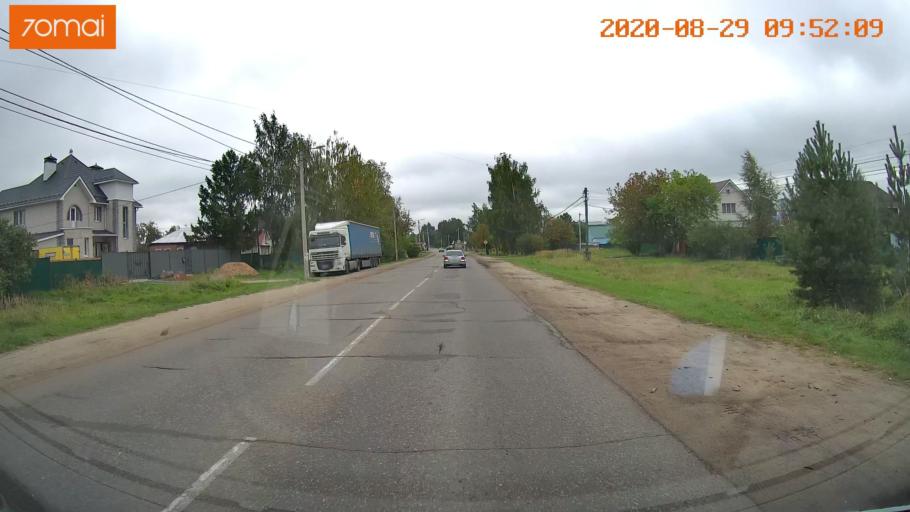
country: RU
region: Ivanovo
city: Kineshma
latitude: 57.4250
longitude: 42.2060
